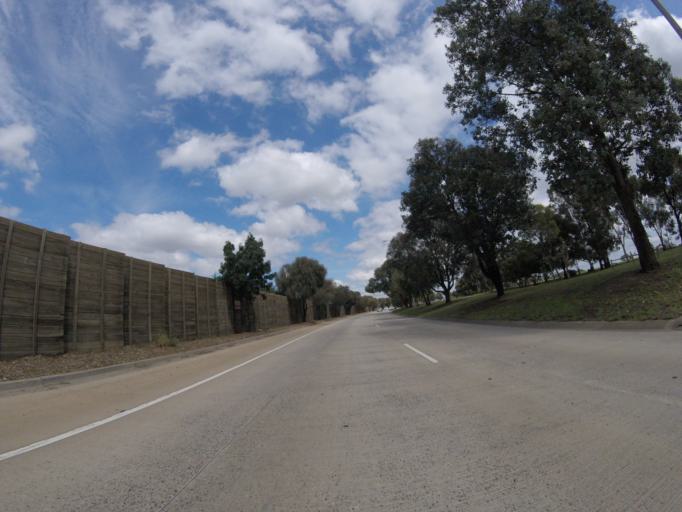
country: AU
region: Victoria
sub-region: Brimbank
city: Keilor Park
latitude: -37.7163
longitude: 144.8582
